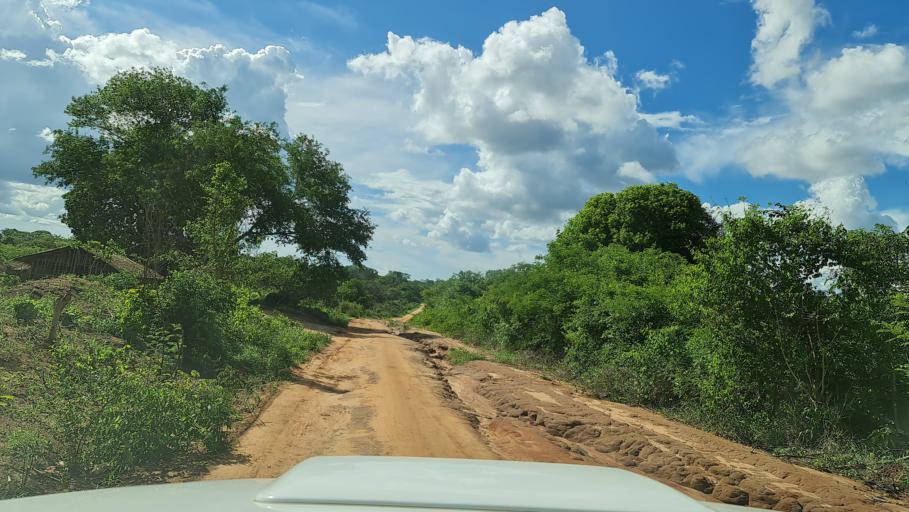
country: MZ
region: Nampula
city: Ilha de Mocambique
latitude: -15.4172
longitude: 40.2609
